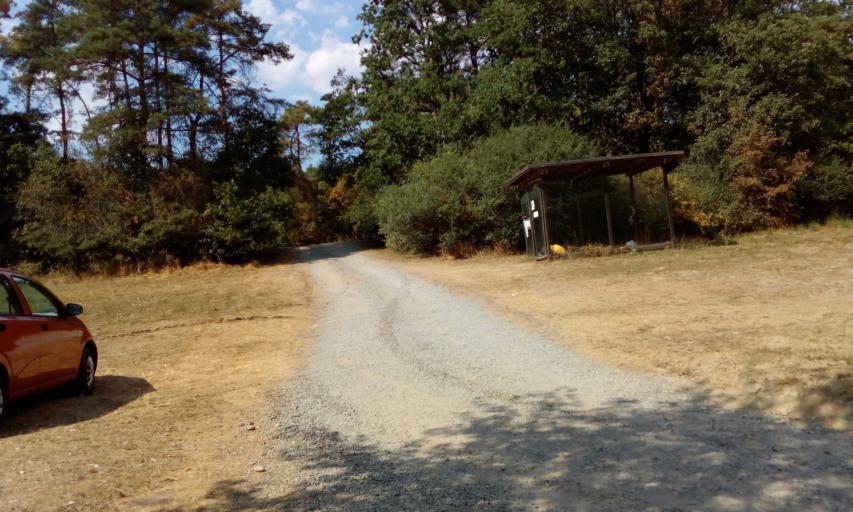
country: BE
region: Wallonia
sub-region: Province du Luxembourg
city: Wellin
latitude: 50.1109
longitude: 5.1343
